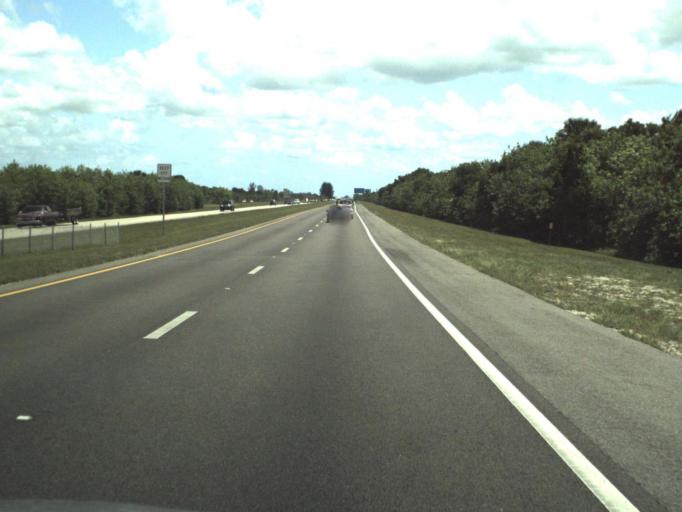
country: US
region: Florida
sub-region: Brevard County
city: Cocoa
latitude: 28.4052
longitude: -80.6927
